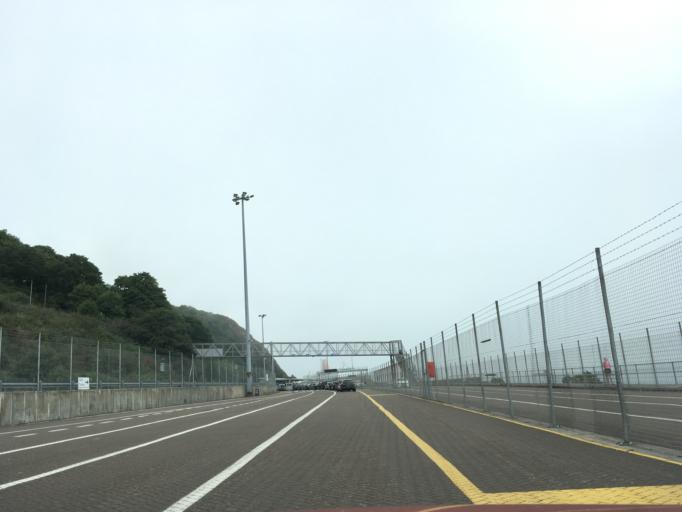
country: GB
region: Wales
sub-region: Pembrokeshire
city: Goodwick
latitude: 52.0057
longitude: -4.9923
